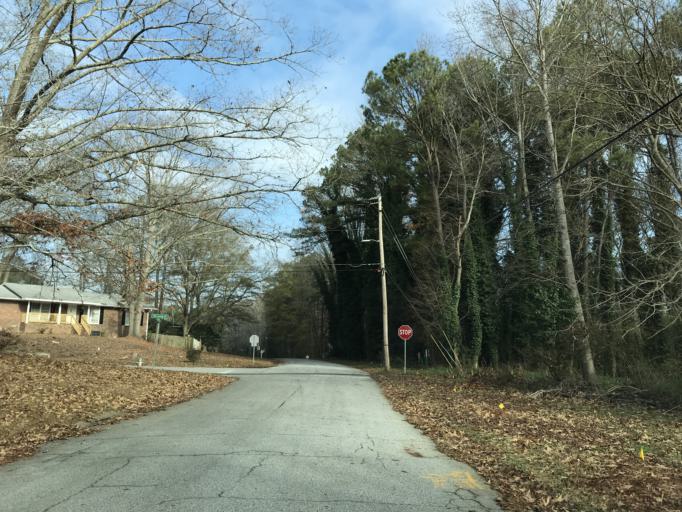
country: US
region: Georgia
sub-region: Clayton County
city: Morrow
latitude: 33.5637
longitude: -84.3631
